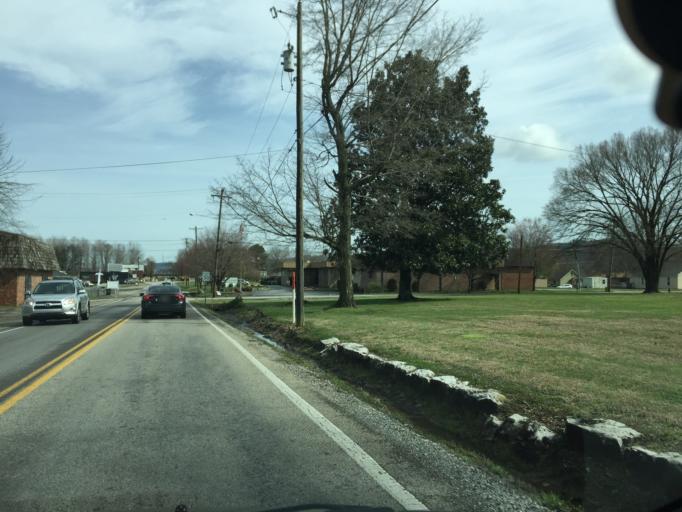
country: US
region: Tennessee
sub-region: Hamilton County
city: Collegedale
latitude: 35.0735
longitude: -85.0639
